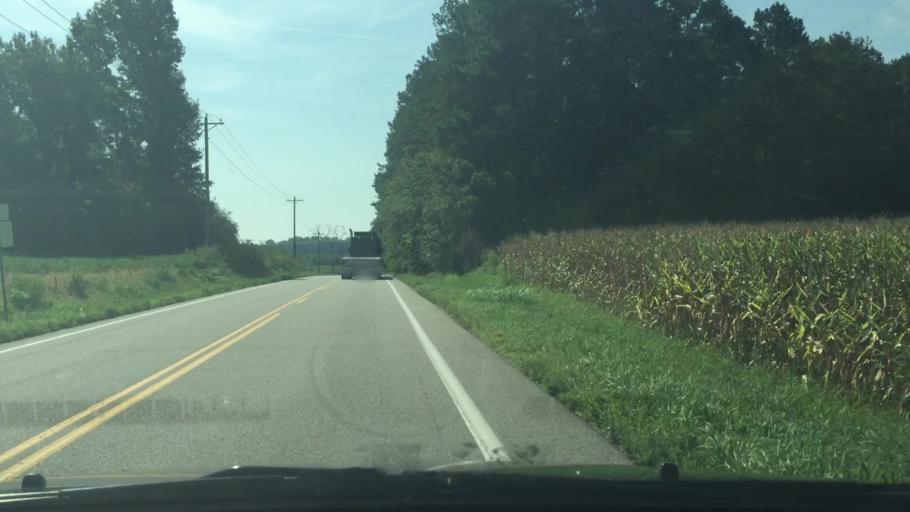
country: US
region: Virginia
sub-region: Sussex County
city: Sussex
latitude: 37.0644
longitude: -77.3336
